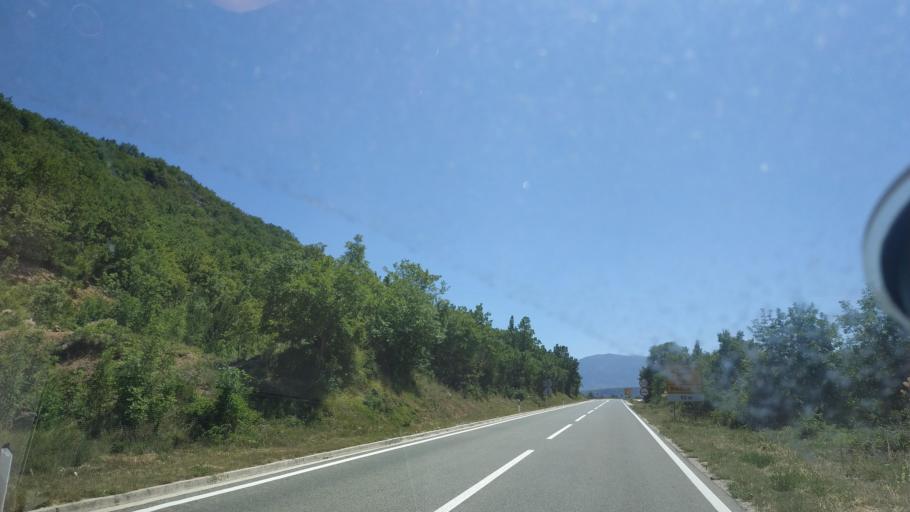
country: HR
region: Sibensko-Kniniska
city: Knin
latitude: 44.0314
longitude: 16.2243
